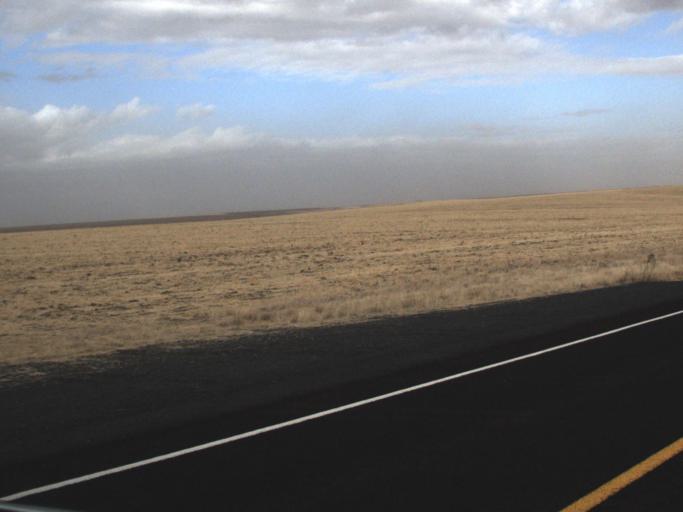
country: US
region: Washington
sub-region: Adams County
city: Ritzville
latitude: 47.3930
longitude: -118.4070
